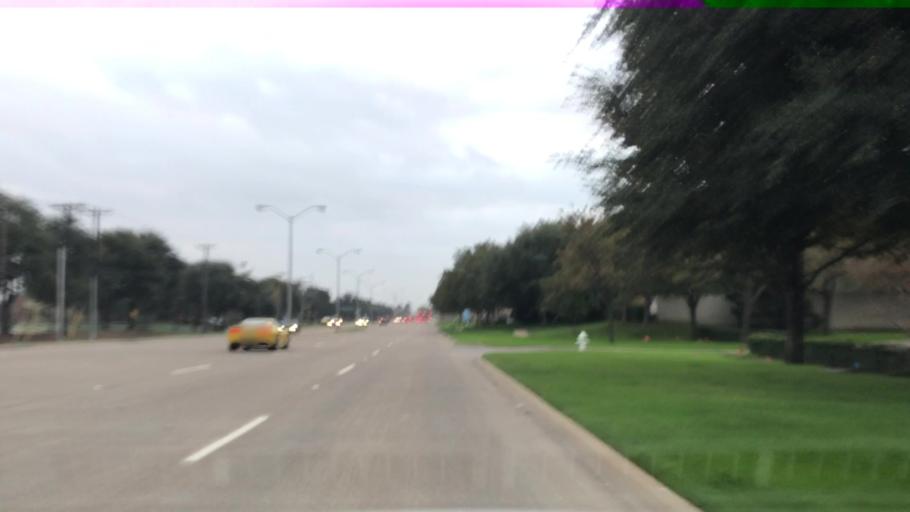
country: US
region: Texas
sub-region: Dallas County
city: Farmers Branch
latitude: 32.9016
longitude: -96.9186
